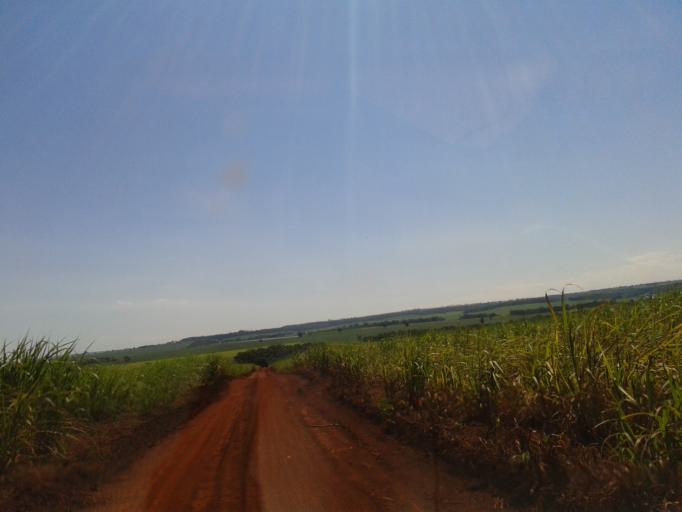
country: BR
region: Minas Gerais
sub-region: Centralina
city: Centralina
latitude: -18.6216
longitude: -49.2610
